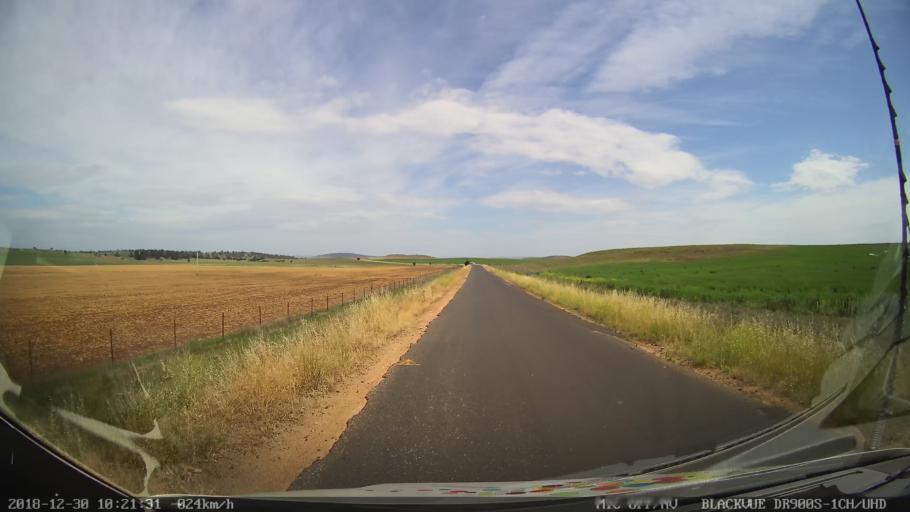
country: AU
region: New South Wales
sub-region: Snowy River
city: Berridale
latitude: -36.5509
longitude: 149.0037
